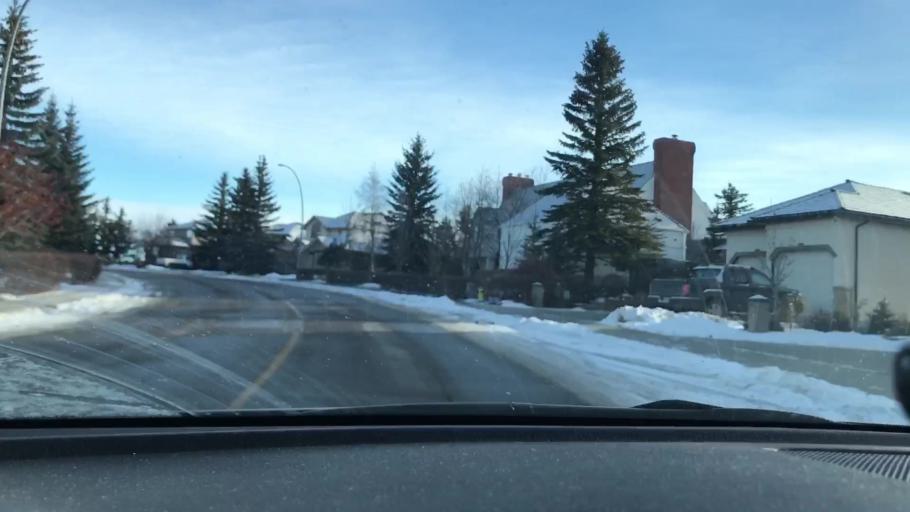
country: CA
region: Alberta
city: Calgary
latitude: 51.0219
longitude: -114.1764
